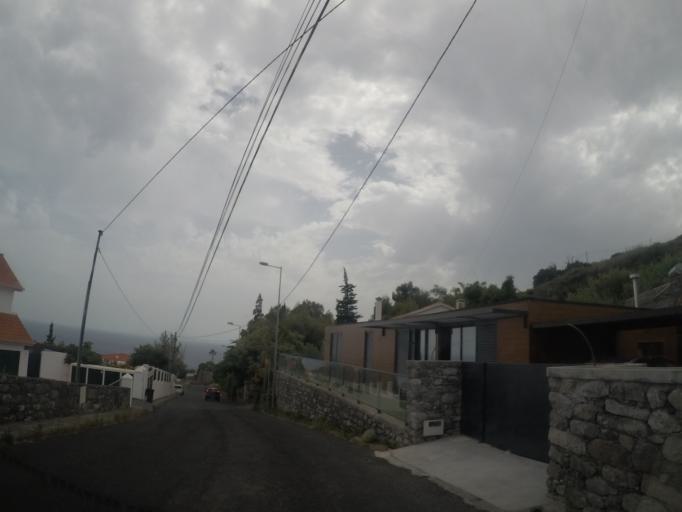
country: PT
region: Madeira
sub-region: Santa Cruz
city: Santa Cruz
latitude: 32.6554
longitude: -16.8177
